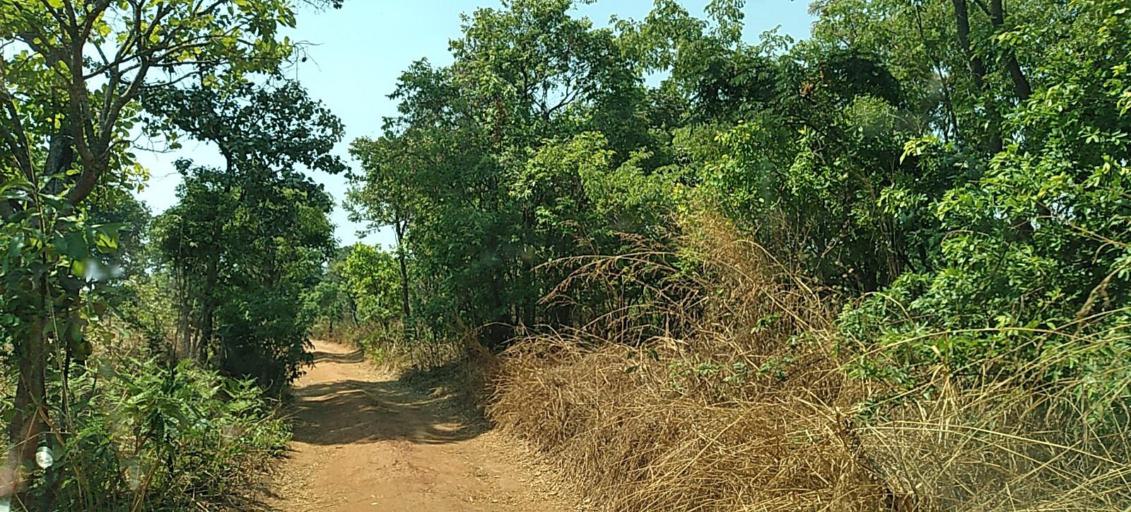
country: ZM
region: North-Western
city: Solwezi
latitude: -12.1046
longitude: 26.2902
